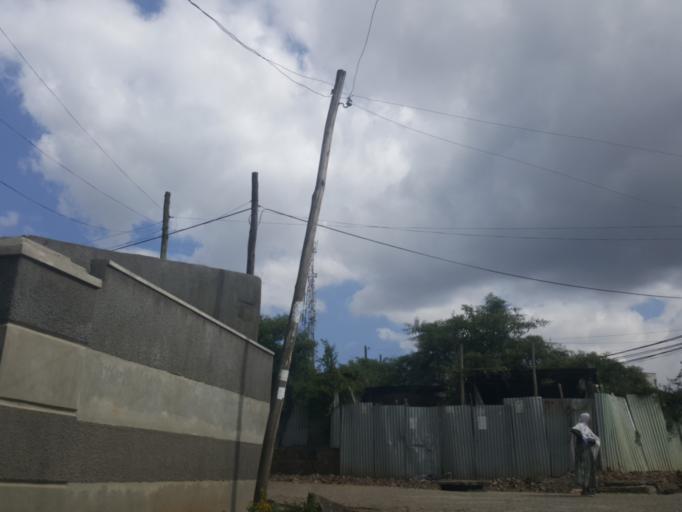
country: ET
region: Adis Abeba
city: Addis Ababa
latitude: 9.0619
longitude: 38.7186
